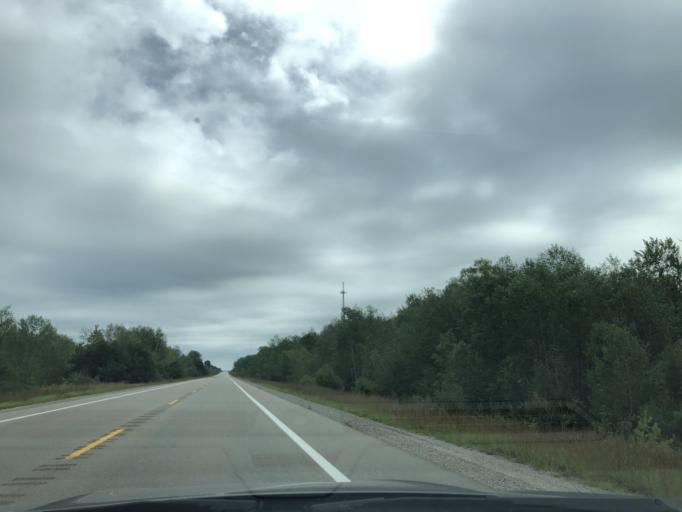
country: US
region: Michigan
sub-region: Clare County
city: Harrison
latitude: 44.0311
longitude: -84.9789
